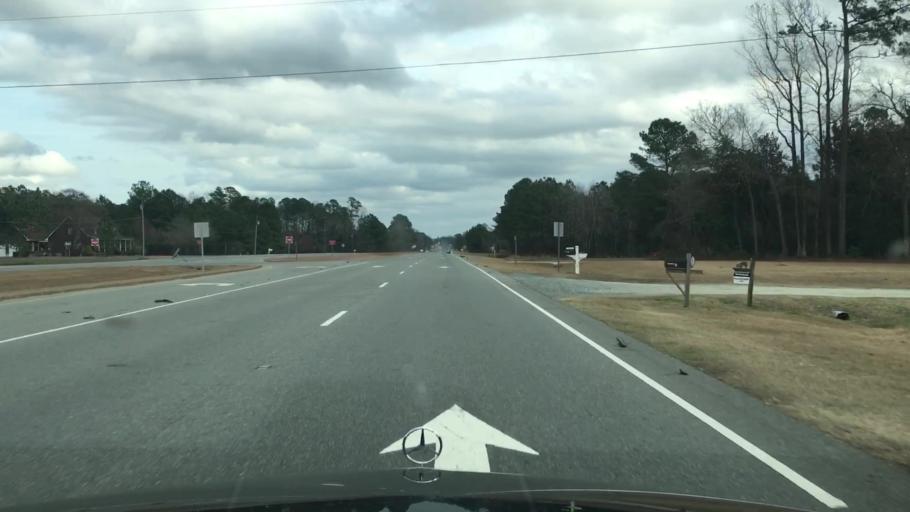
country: US
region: North Carolina
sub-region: Duplin County
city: Beulaville
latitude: 34.9298
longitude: -77.8137
